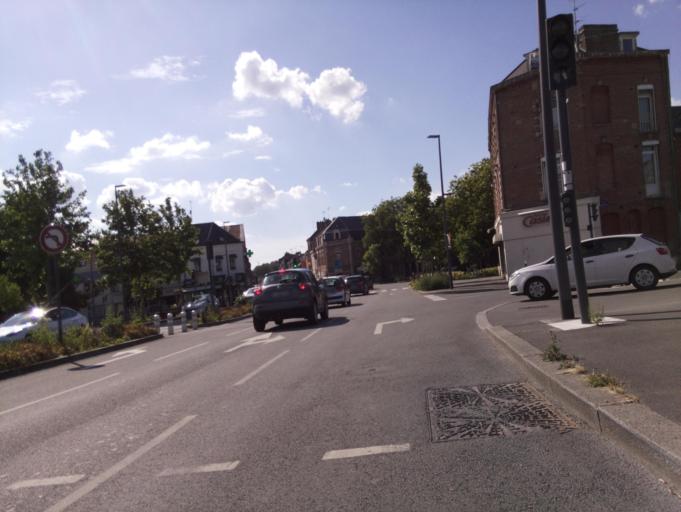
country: FR
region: Picardie
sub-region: Departement de la Somme
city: Amiens
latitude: 49.8939
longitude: 2.2848
